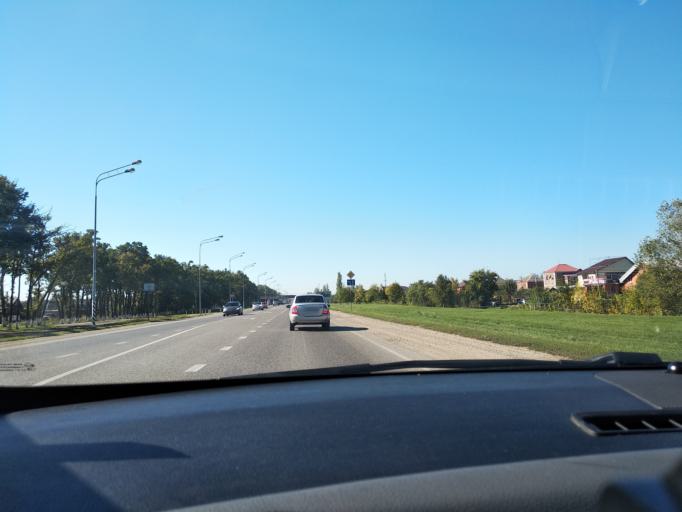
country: RU
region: Krasnodarskiy
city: Krasnodar
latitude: 45.1390
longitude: 39.0356
